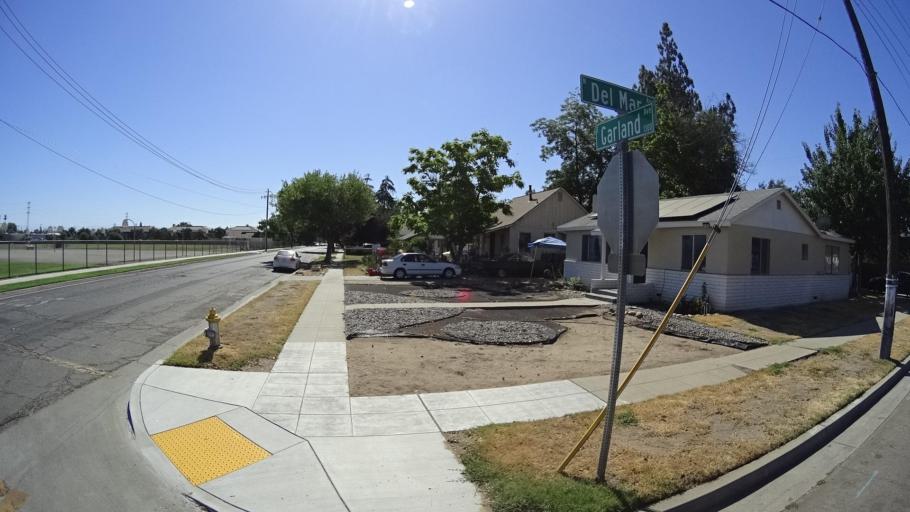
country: US
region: California
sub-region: Fresno County
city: Fresno
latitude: 36.7849
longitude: -119.7951
